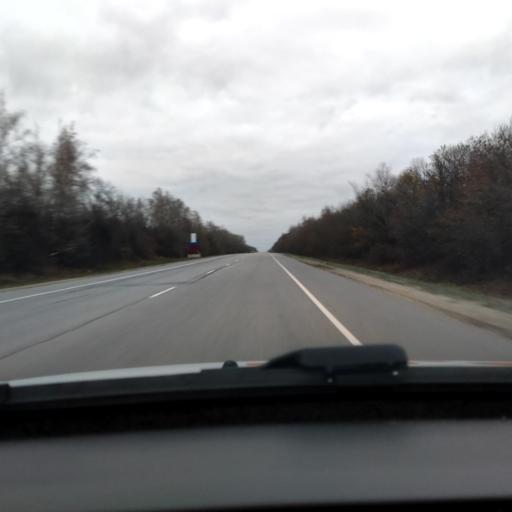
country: RU
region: Lipetsk
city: Khlevnoye
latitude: 52.3424
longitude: 39.1857
